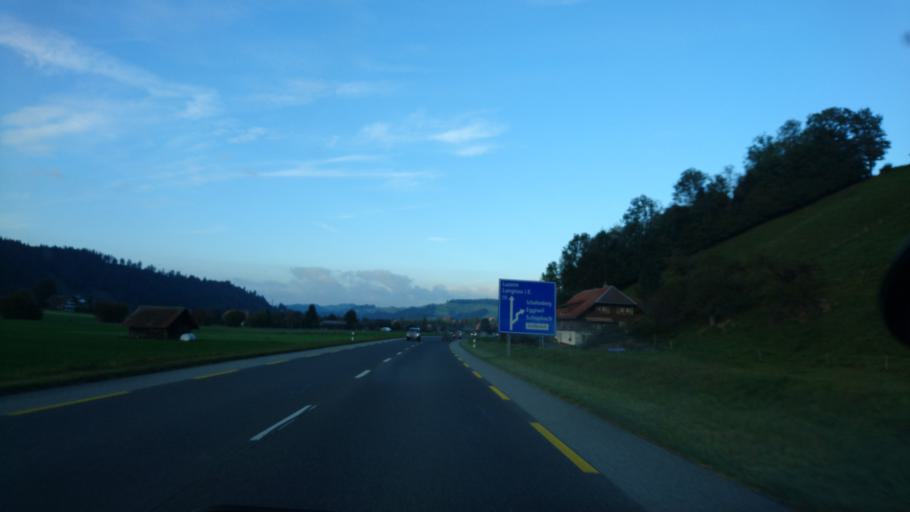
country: CH
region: Bern
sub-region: Emmental District
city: Signau
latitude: 46.9215
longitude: 7.7331
